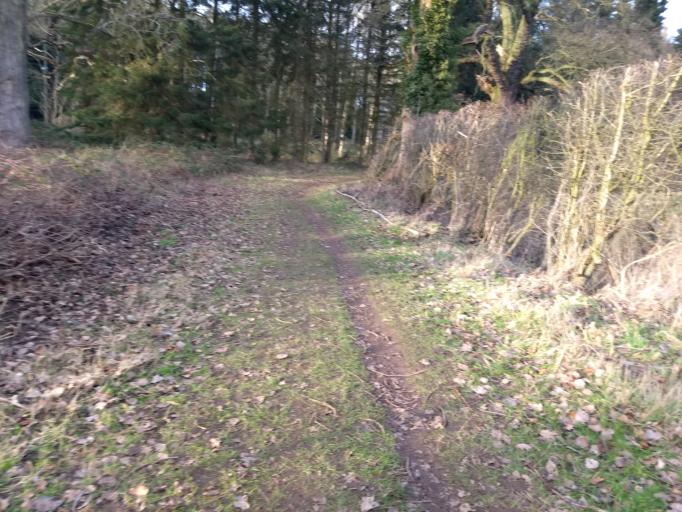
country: GB
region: England
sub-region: Central Bedfordshire
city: Woburn
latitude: 51.9890
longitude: -0.6368
